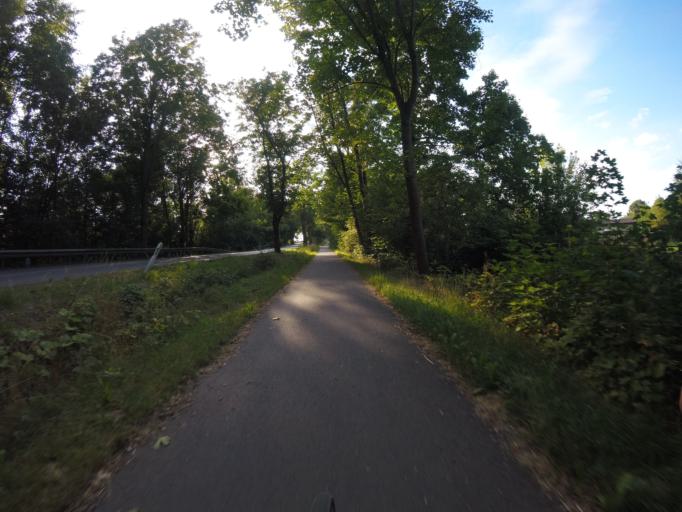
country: DE
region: Brandenburg
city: Altlandsberg
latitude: 52.5630
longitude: 13.7548
